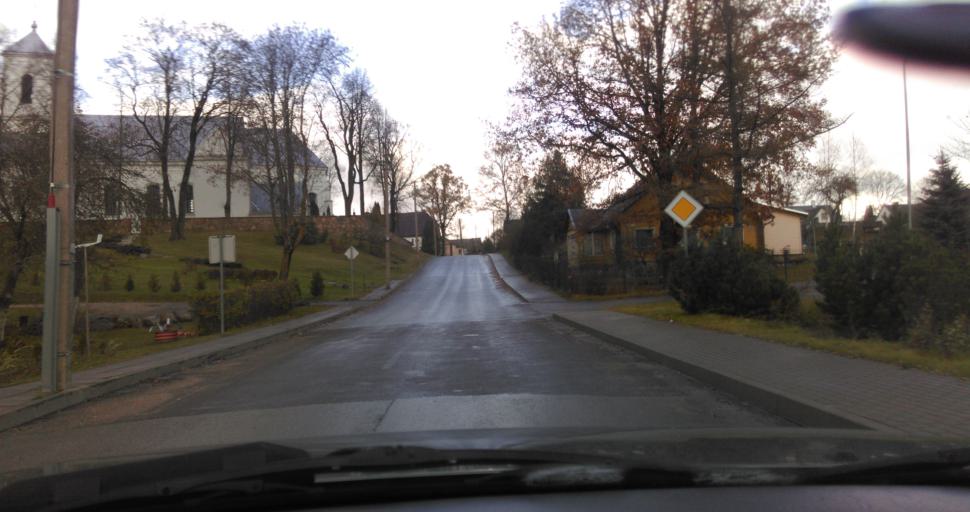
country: LT
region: Utenos apskritis
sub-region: Utena
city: Utena
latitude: 55.5846
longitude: 25.4953
